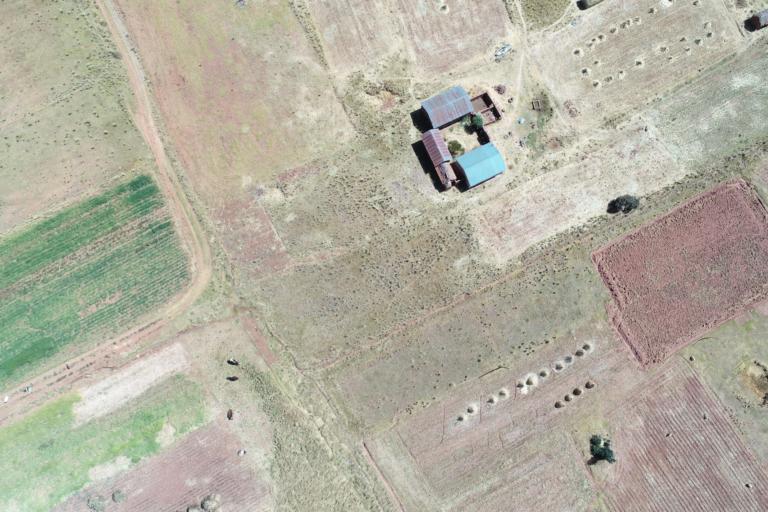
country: BO
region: La Paz
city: Tiahuanaco
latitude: -16.6019
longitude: -68.7717
